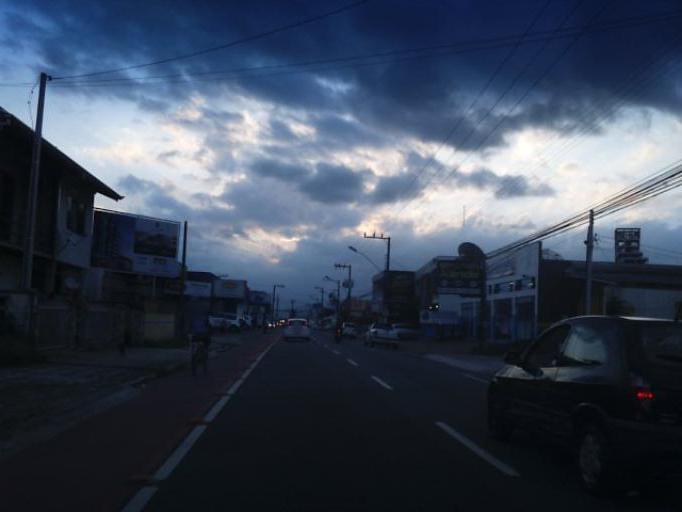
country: BR
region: Santa Catarina
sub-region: Itajai
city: Itajai
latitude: -26.9094
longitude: -48.6808
